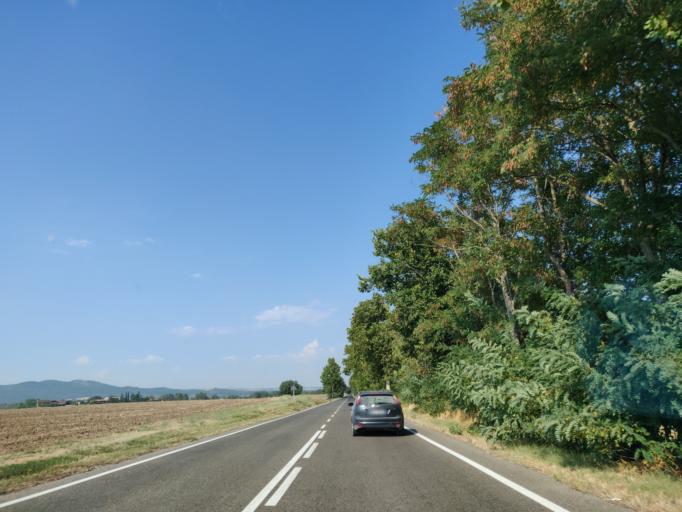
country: IT
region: Latium
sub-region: Provincia di Viterbo
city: Montalto di Castro
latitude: 42.3913
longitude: 11.6673
